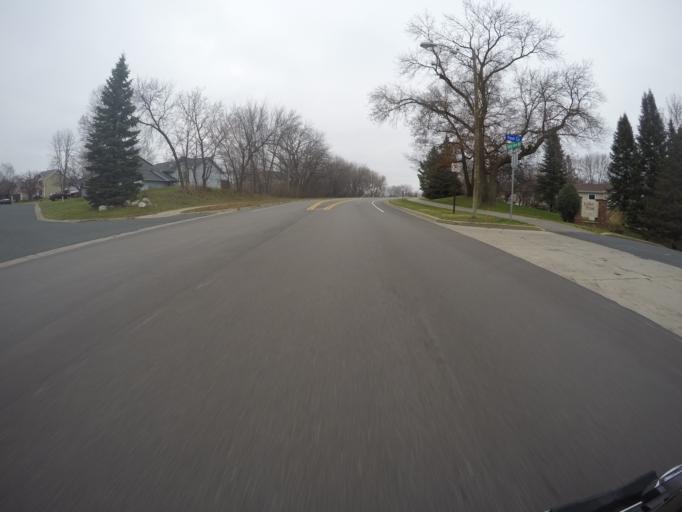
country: US
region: Minnesota
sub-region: Carver County
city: Chanhassen
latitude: 44.8735
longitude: -93.5003
